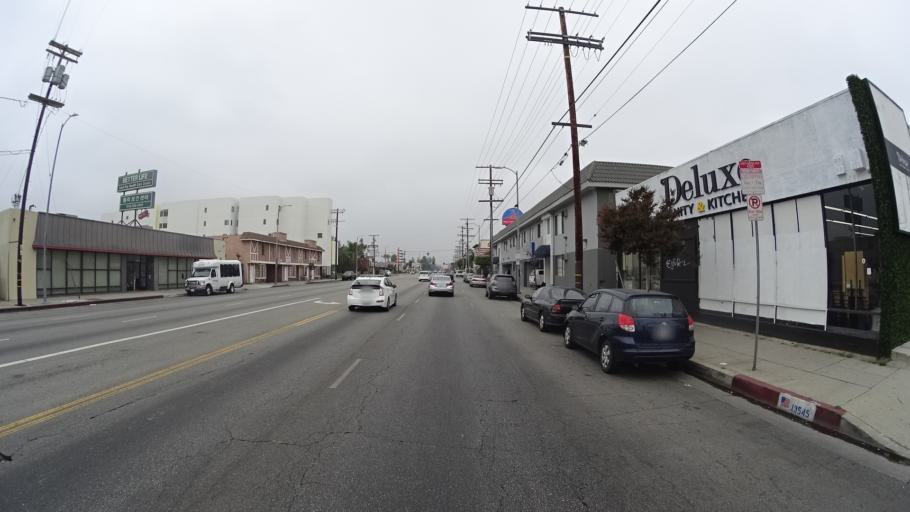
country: US
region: California
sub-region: Los Angeles County
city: Van Nuys
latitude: 34.2012
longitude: -118.4281
